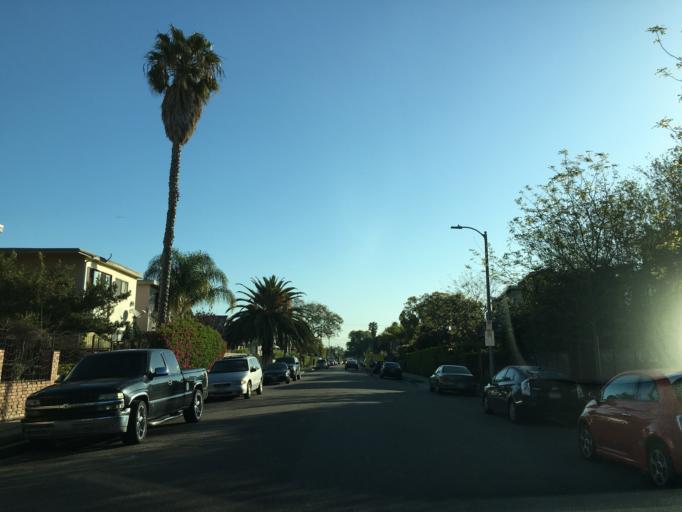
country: US
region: California
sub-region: Los Angeles County
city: Marina del Rey
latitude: 33.9945
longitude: -118.4705
